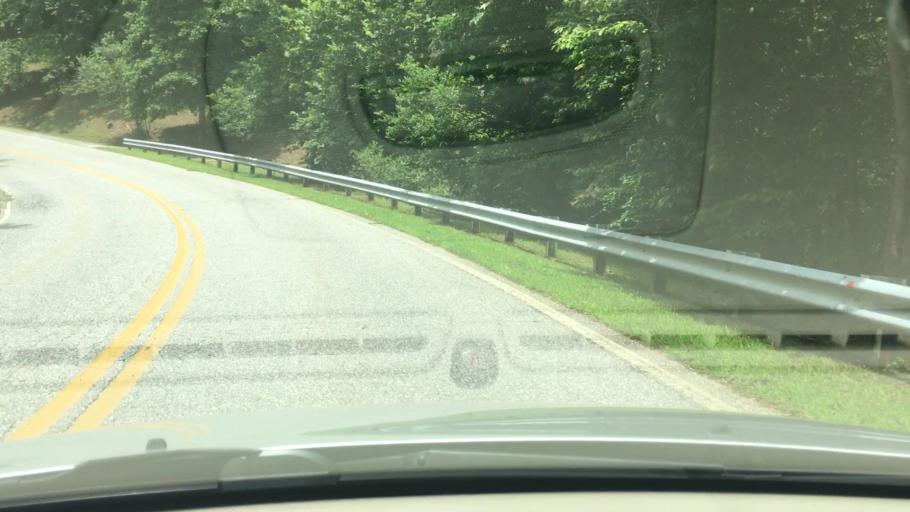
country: US
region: Georgia
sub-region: Dawson County
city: Dawsonville
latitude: 34.5690
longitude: -84.2440
